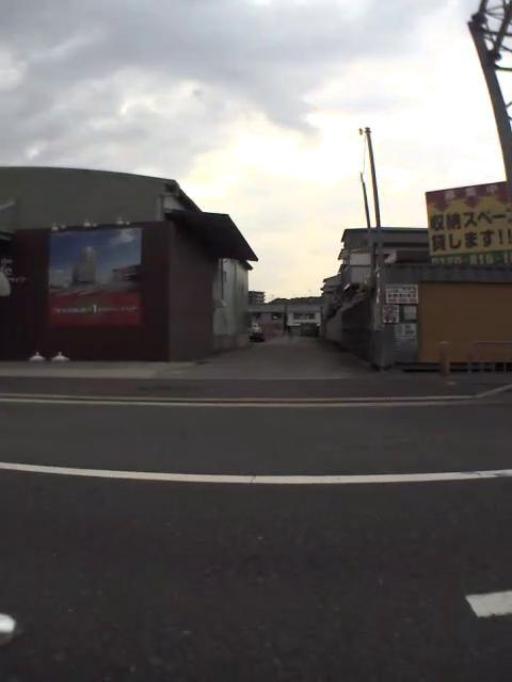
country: JP
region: Osaka
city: Hirakata
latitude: 34.8039
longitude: 135.6319
